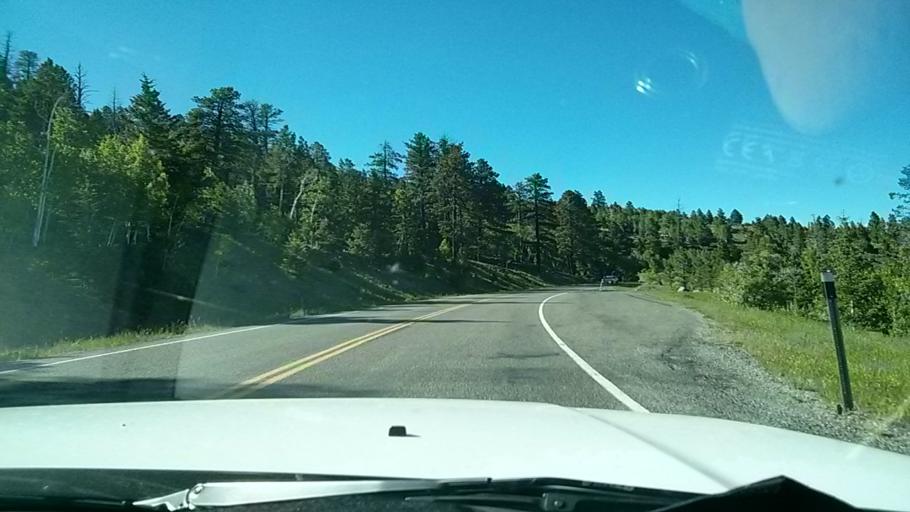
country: US
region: Utah
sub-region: Wayne County
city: Loa
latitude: 38.1225
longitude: -111.3301
